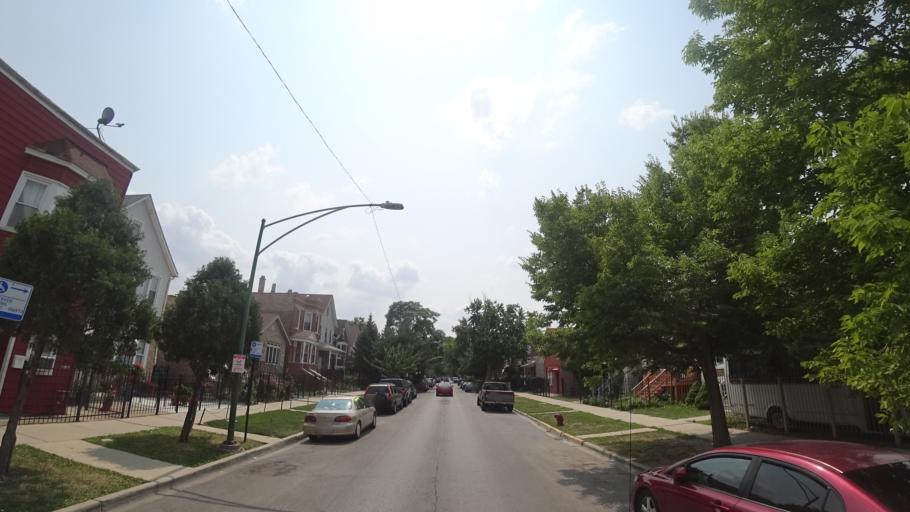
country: US
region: Illinois
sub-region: Cook County
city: Cicero
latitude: 41.8434
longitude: -87.7294
